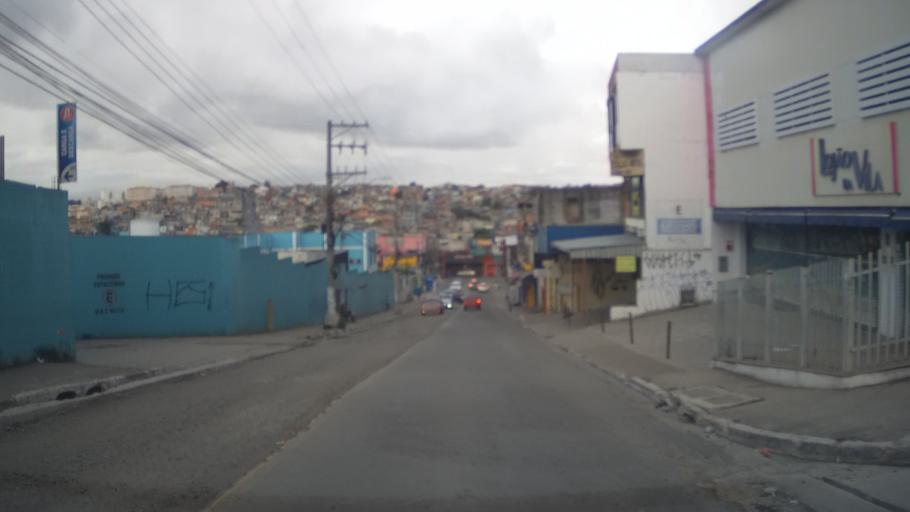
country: BR
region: Sao Paulo
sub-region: Itaquaquecetuba
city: Itaquaquecetuba
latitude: -23.4449
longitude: -46.4096
